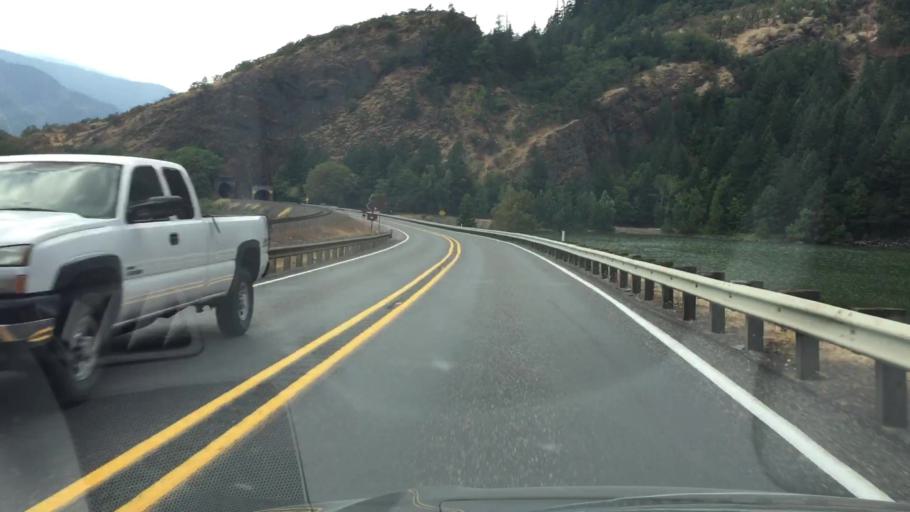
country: US
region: Oregon
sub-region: Hood River County
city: Hood River
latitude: 45.7174
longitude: -121.6133
